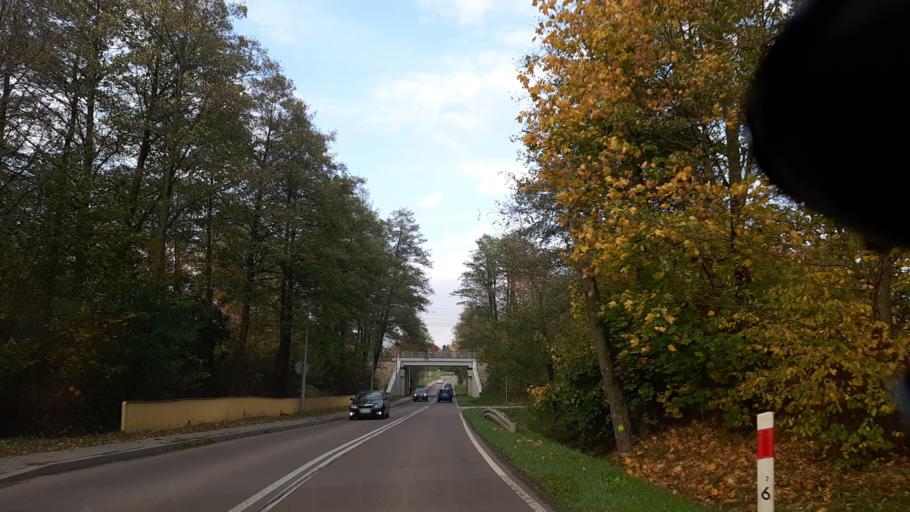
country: PL
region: Lublin Voivodeship
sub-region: Powiat pulawski
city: Naleczow
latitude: 51.3162
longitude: 22.2215
